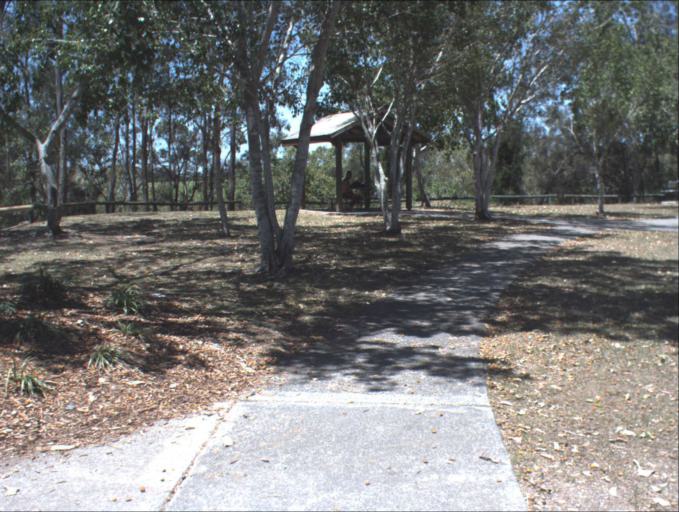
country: AU
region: Queensland
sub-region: Gold Coast
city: Yatala
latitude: -27.7138
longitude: 153.2125
